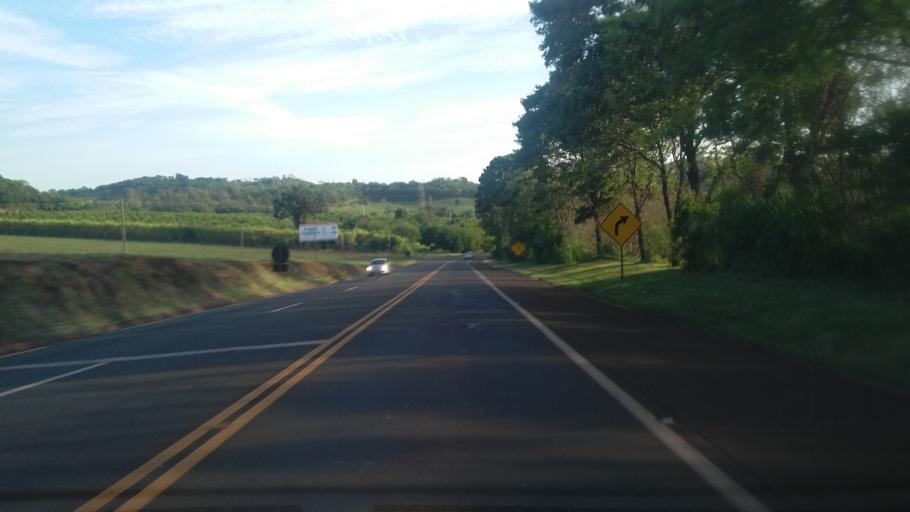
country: BR
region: Parana
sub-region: Assai
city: Assai
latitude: -23.2152
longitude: -50.6693
